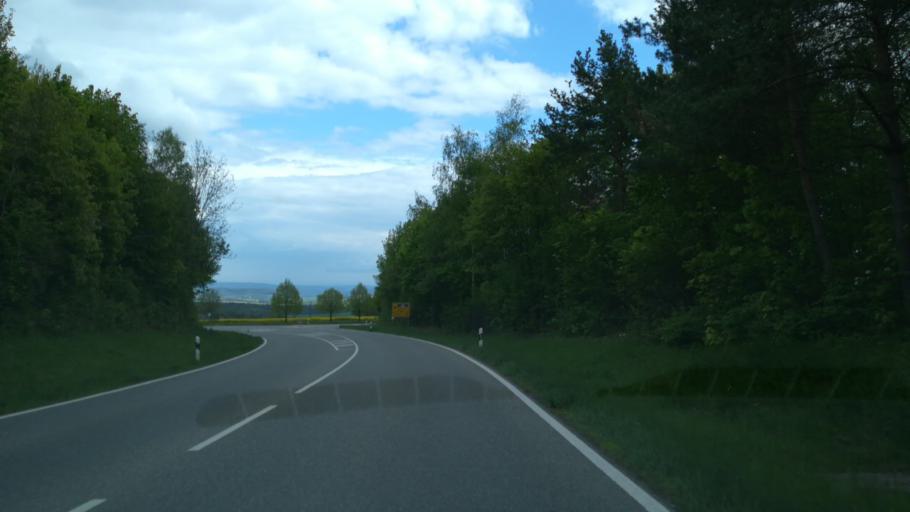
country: DE
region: Baden-Wuerttemberg
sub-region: Freiburg Region
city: Tengen
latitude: 47.8203
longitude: 8.6422
